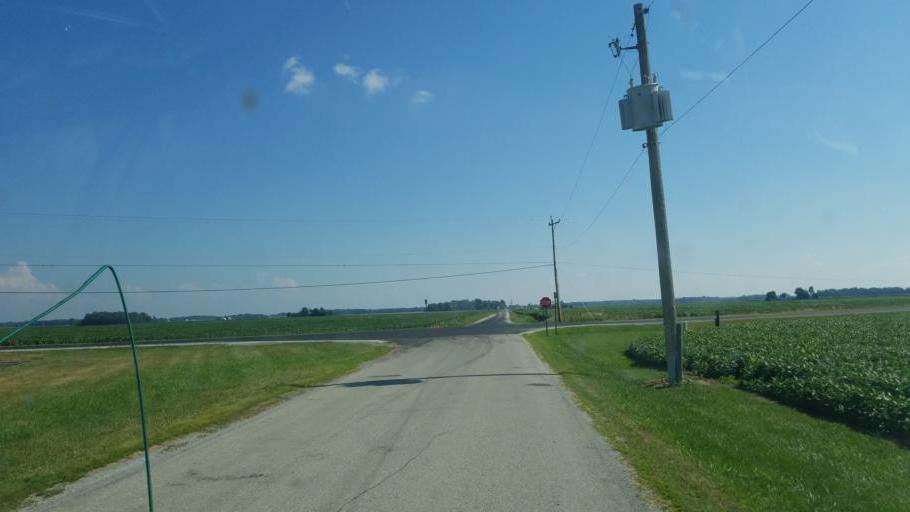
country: US
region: Ohio
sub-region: Hardin County
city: Kenton
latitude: 40.6804
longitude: -83.5145
